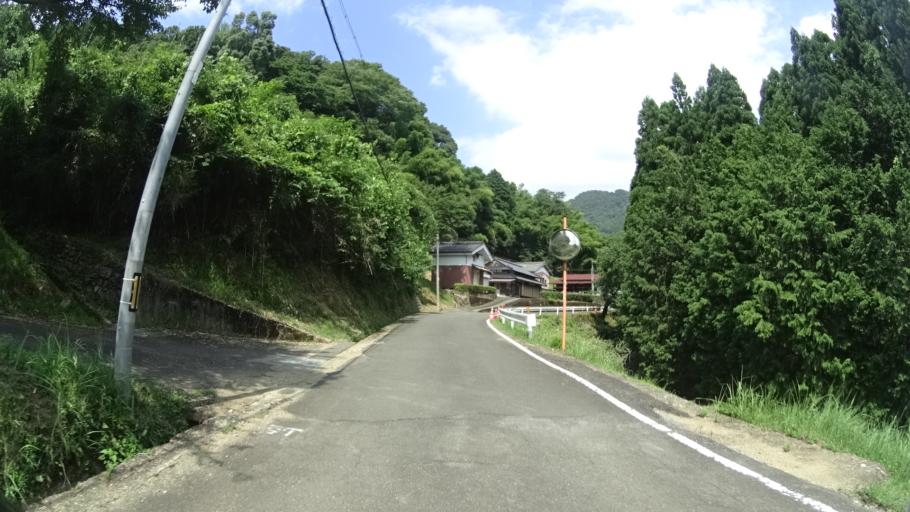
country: JP
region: Kyoto
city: Maizuru
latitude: 35.3845
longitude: 135.3572
